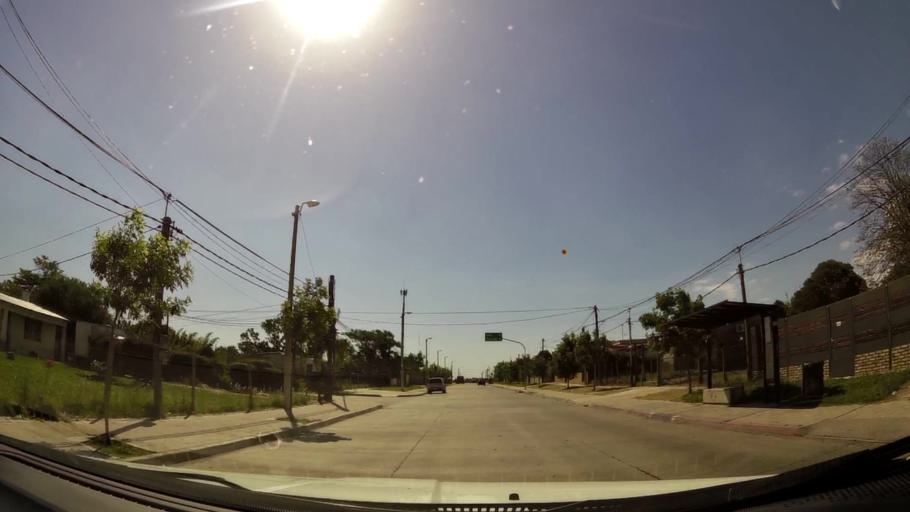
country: UY
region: Canelones
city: La Paz
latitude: -34.8381
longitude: -56.2499
